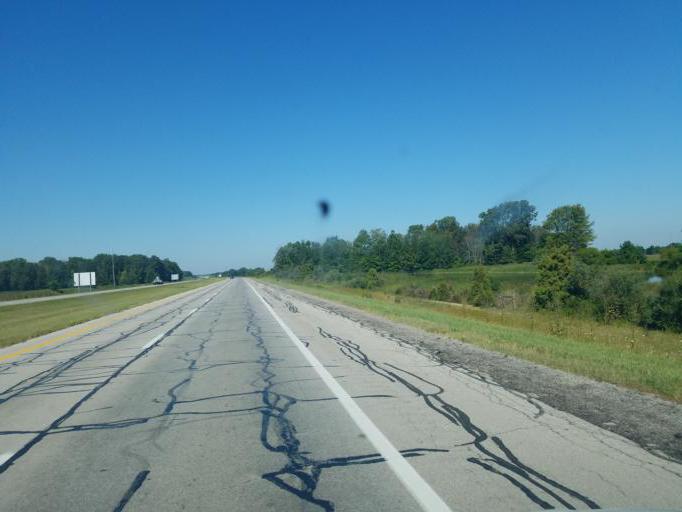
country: US
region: Ohio
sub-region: Crawford County
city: Bucyrus
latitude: 40.8273
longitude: -82.9937
